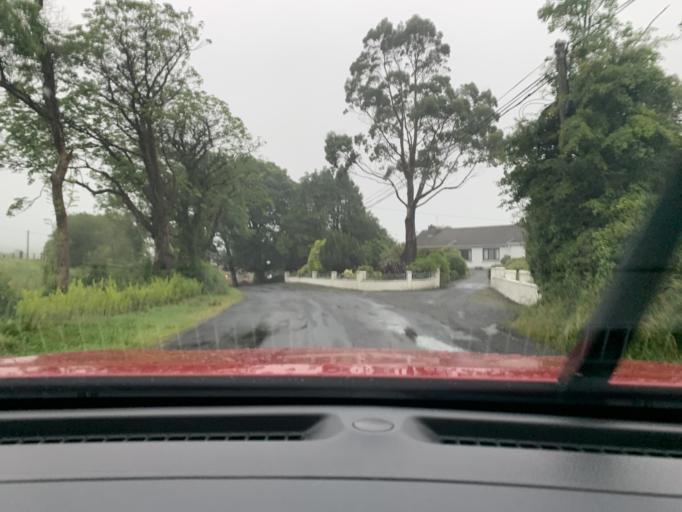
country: IE
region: Connaught
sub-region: Sligo
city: Sligo
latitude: 54.3276
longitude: -8.4219
